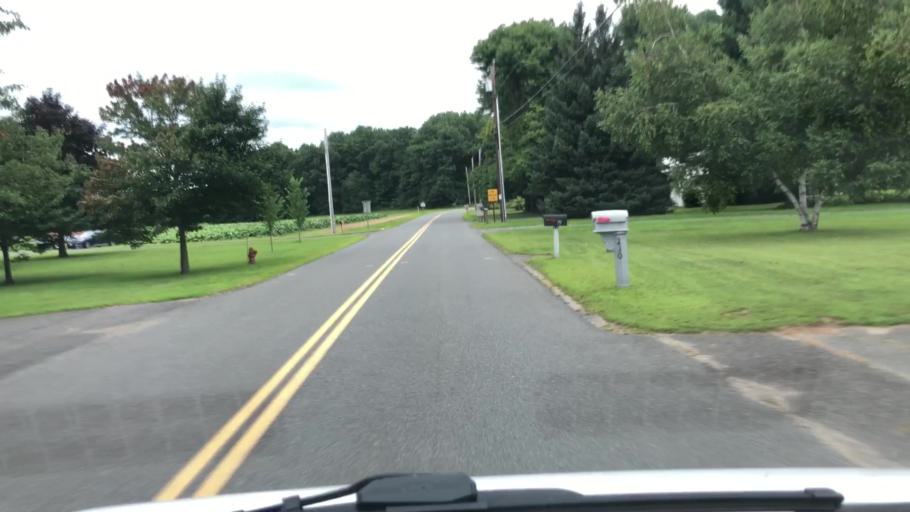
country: US
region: Massachusetts
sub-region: Franklin County
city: South Deerfield
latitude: 42.4516
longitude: -72.6080
